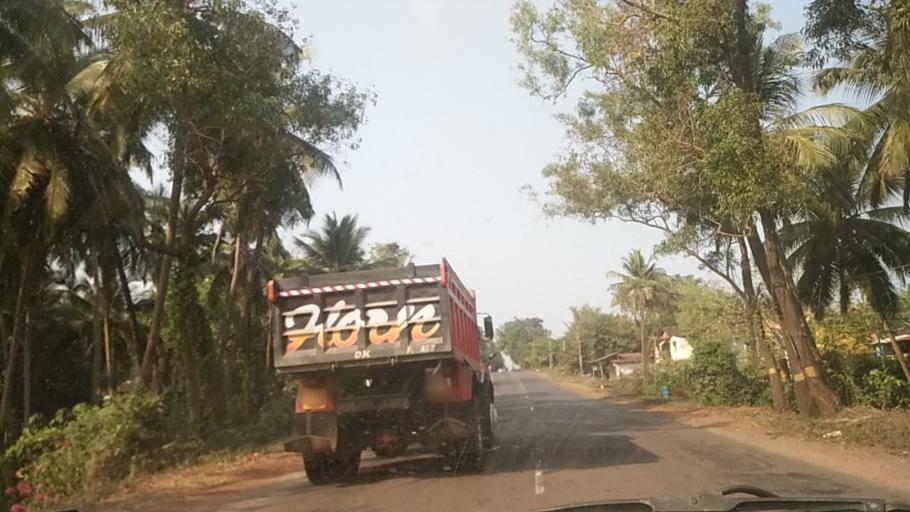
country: IN
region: Goa
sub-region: North Goa
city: Colovale
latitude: 15.6572
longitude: 73.8391
